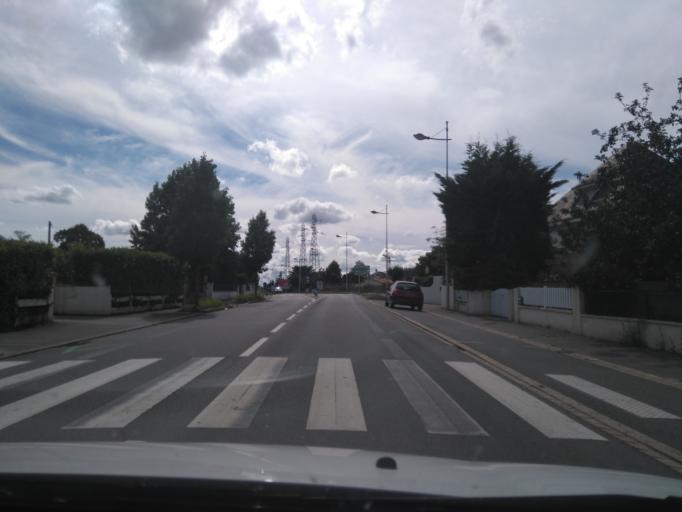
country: FR
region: Pays de la Loire
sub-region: Departement de la Loire-Atlantique
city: Reze
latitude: 47.1720
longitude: -1.5729
